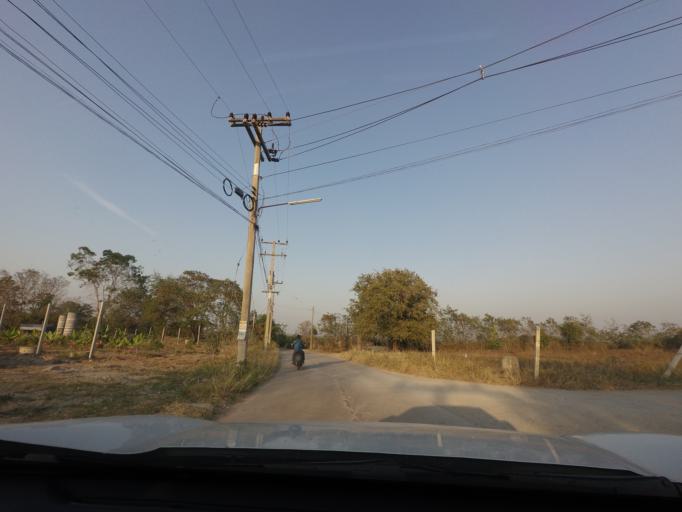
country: TH
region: Nakhon Ratchasima
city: Pak Chong
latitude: 14.6473
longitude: 101.3813
